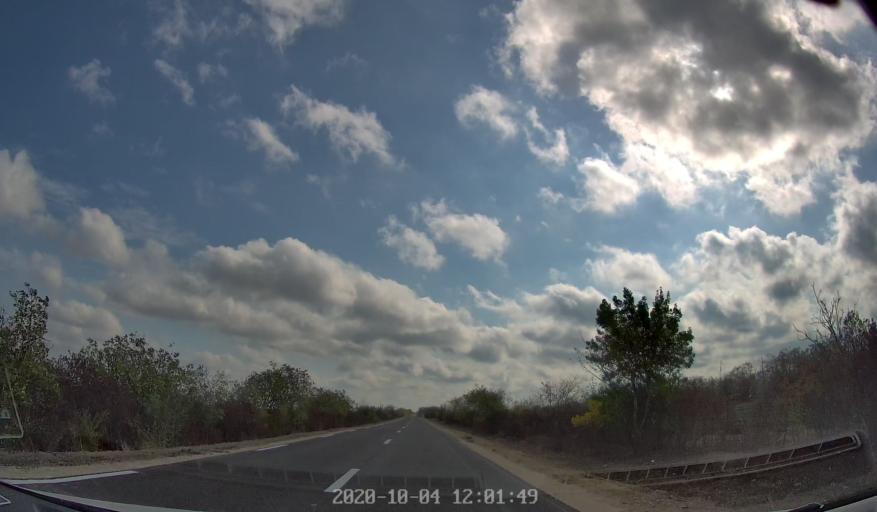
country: MD
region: Rezina
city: Saharna
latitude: 47.6219
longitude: 28.8955
